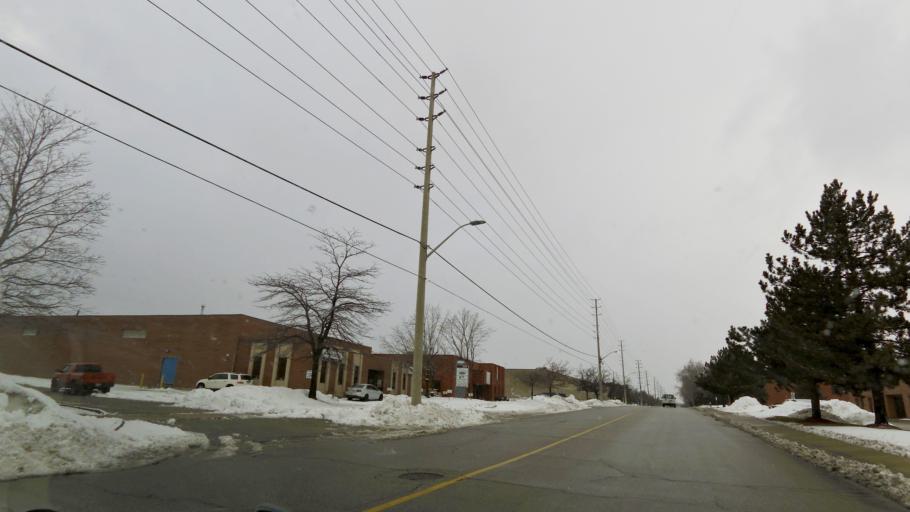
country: CA
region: Ontario
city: Mississauga
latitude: 43.6545
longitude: -79.6615
